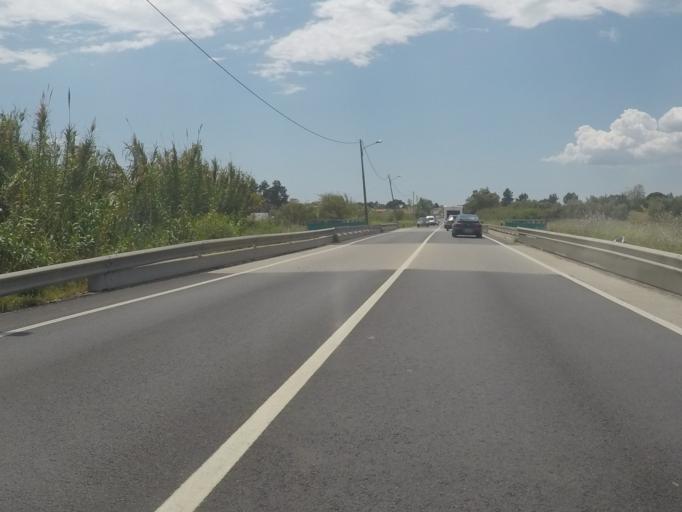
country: PT
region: Setubal
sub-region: Setubal
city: Setubal
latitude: 38.5491
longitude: -8.8125
